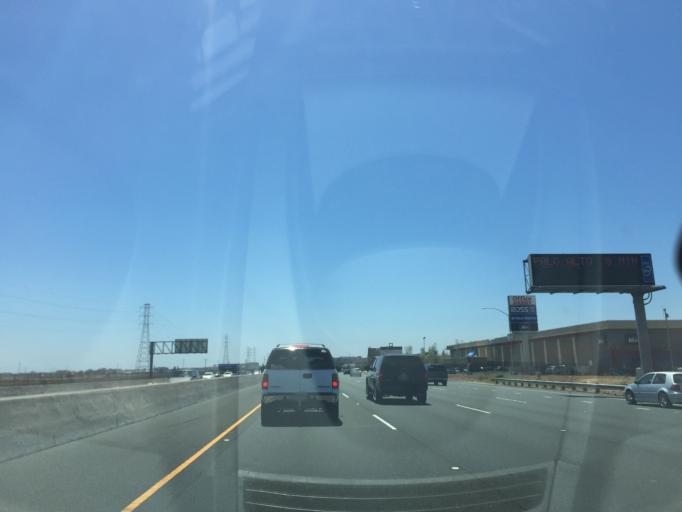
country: US
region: California
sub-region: San Mateo County
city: San Carlos
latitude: 37.5056
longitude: -122.2468
